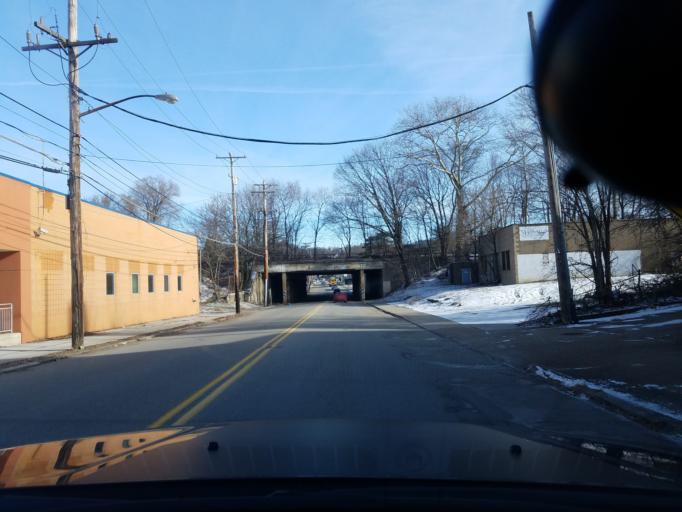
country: US
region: Pennsylvania
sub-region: Allegheny County
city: Wilkinsburg
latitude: 40.4493
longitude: -79.8935
